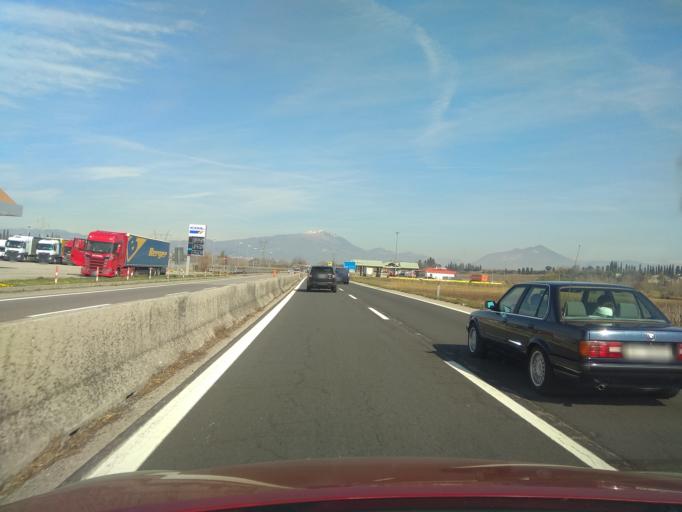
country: IT
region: Veneto
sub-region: Provincia di Verona
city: Cola
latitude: 45.4773
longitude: 10.7638
